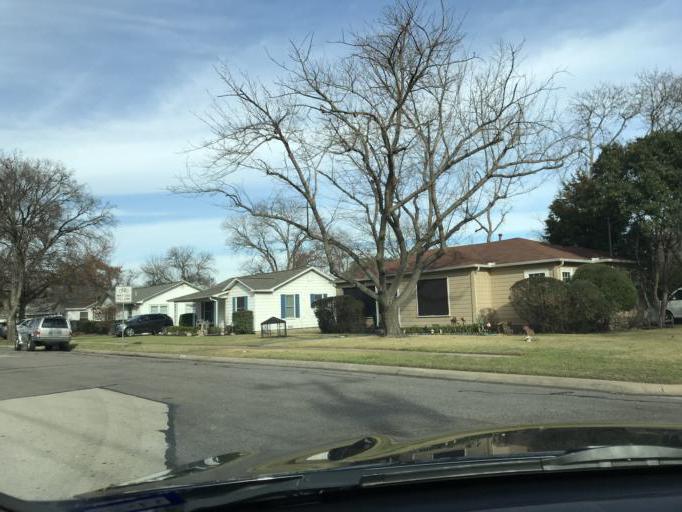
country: US
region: Texas
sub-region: Denton County
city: Denton
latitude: 33.2276
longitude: -97.1379
